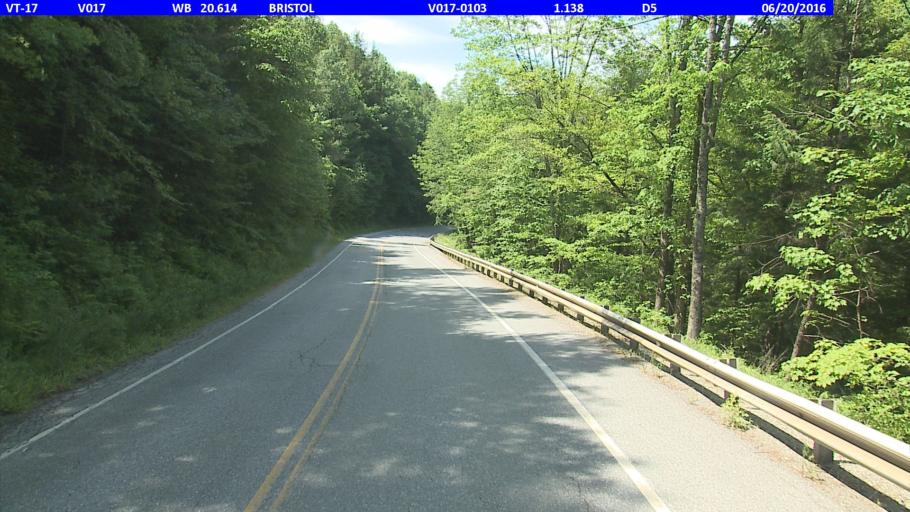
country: US
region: Vermont
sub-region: Addison County
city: Bristol
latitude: 44.1594
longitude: -73.0396
